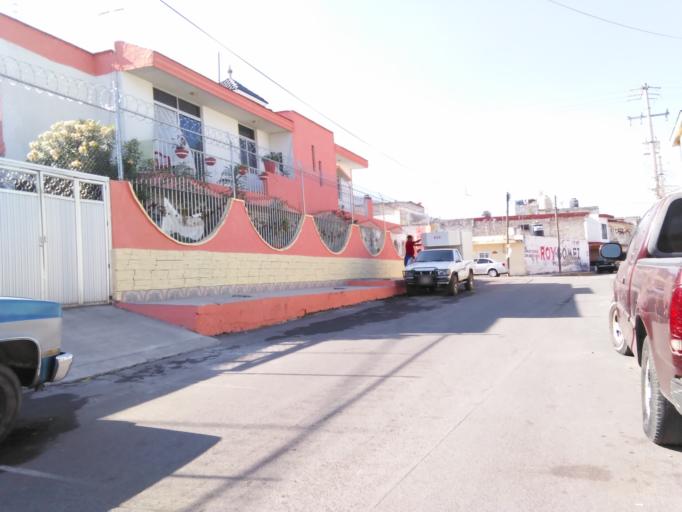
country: MX
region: Nayarit
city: Tepic
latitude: 21.4919
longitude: -104.8985
